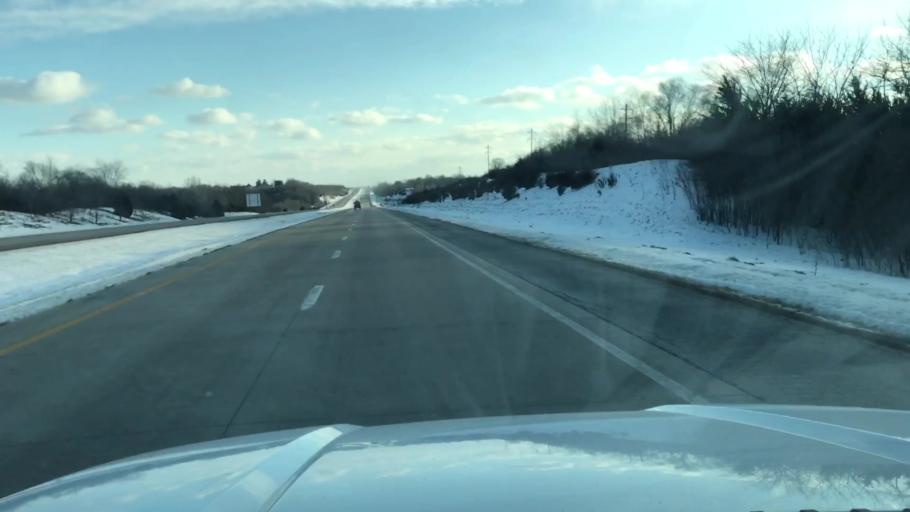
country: US
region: Missouri
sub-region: Andrew County
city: Savannah
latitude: 39.9459
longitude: -94.8604
